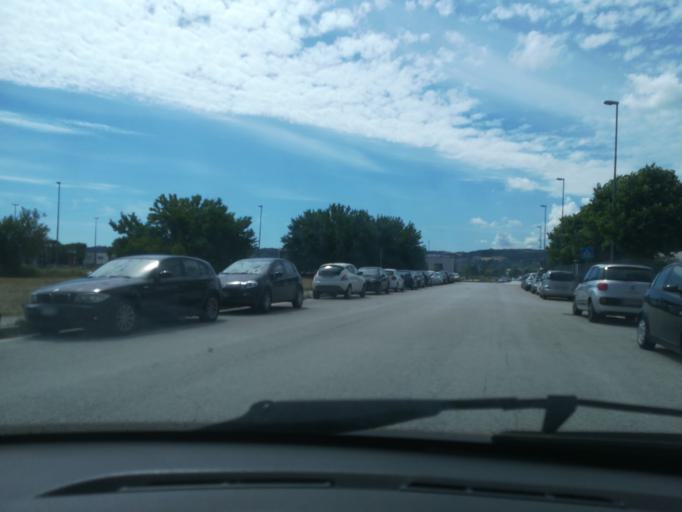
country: IT
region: The Marches
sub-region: Provincia di Macerata
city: Santa Maria Apparente
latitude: 43.2881
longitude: 13.6795
